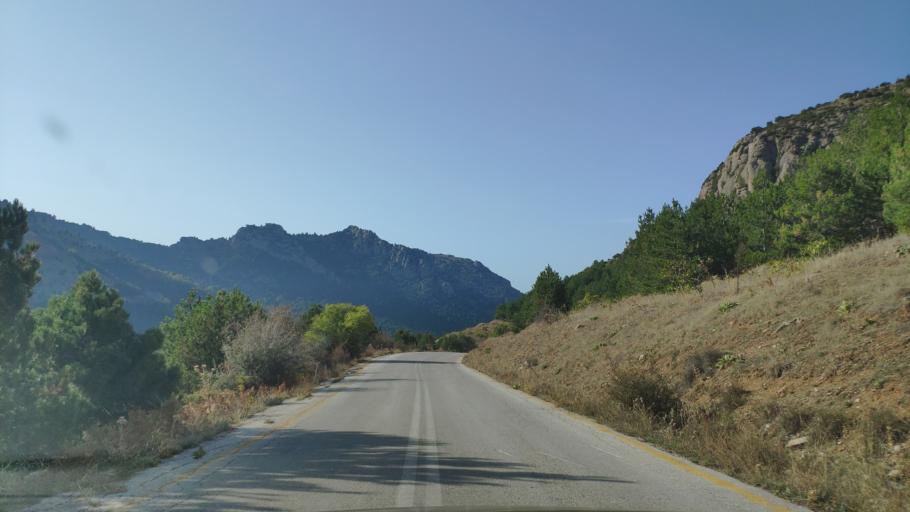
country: GR
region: West Greece
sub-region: Nomos Achaias
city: Aiyira
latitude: 38.0428
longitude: 22.3914
